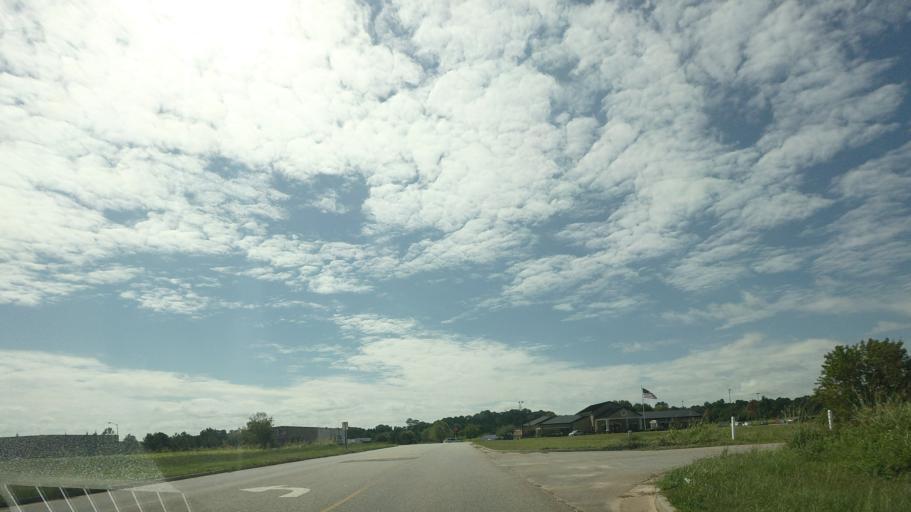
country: US
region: Georgia
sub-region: Houston County
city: Centerville
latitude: 32.6143
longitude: -83.6952
